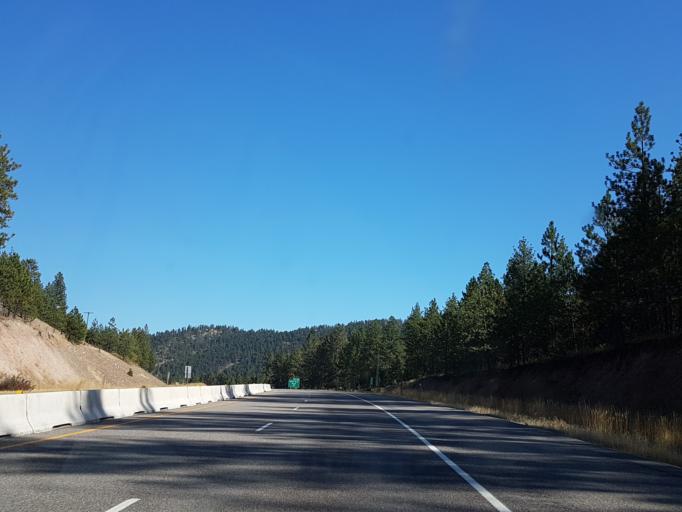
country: US
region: Montana
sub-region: Missoula County
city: Frenchtown
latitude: 47.0196
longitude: -114.3767
